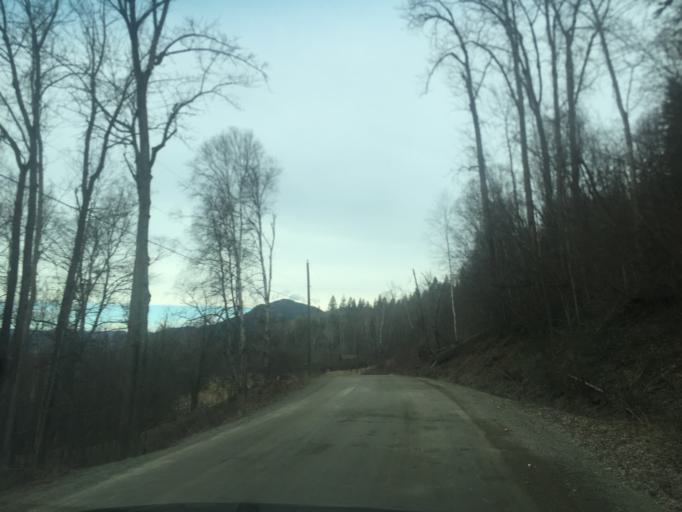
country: CA
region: British Columbia
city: Kamloops
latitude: 51.3340
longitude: -120.1492
